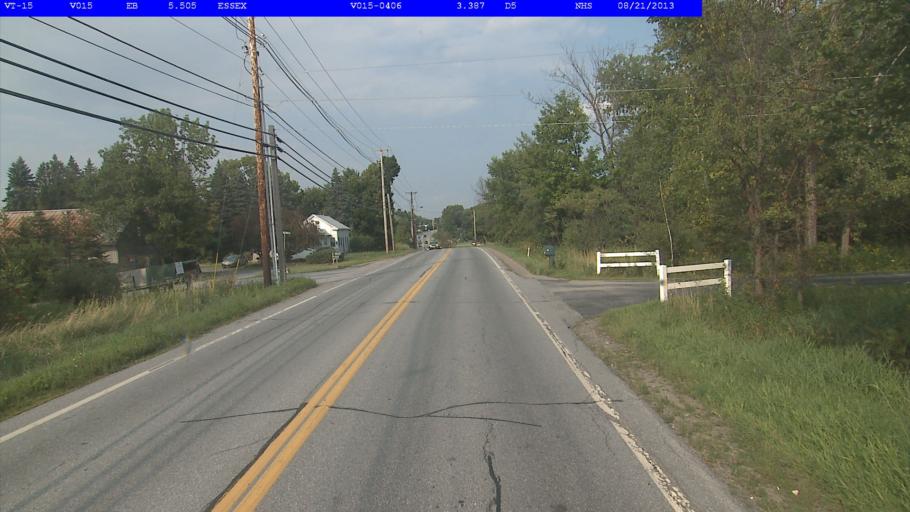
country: US
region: Vermont
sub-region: Chittenden County
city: Essex Junction
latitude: 44.5025
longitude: -73.0948
